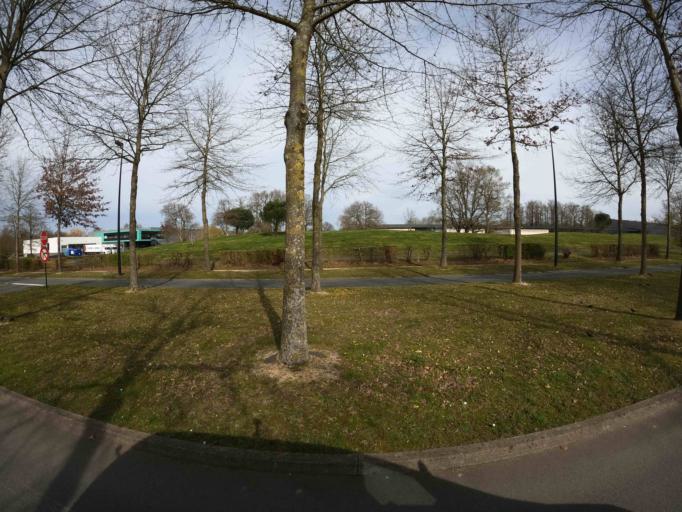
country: FR
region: Pays de la Loire
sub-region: Departement de la Vendee
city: Bouffere
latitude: 46.9543
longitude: -1.3516
